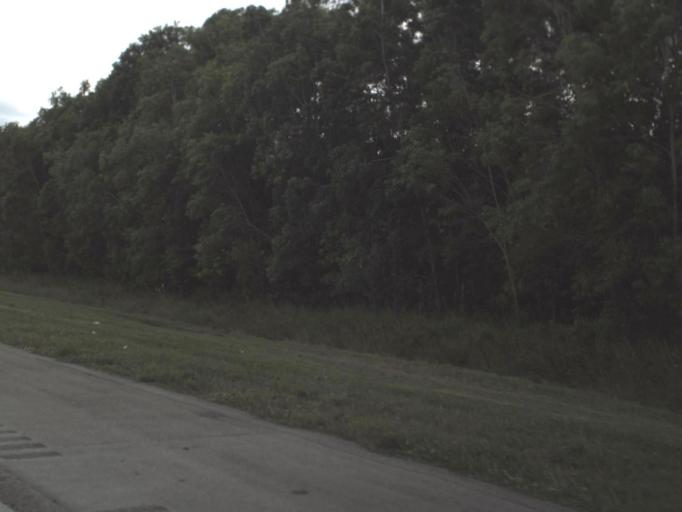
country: US
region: Florida
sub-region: Saint Lucie County
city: White City
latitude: 27.3535
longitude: -80.3746
